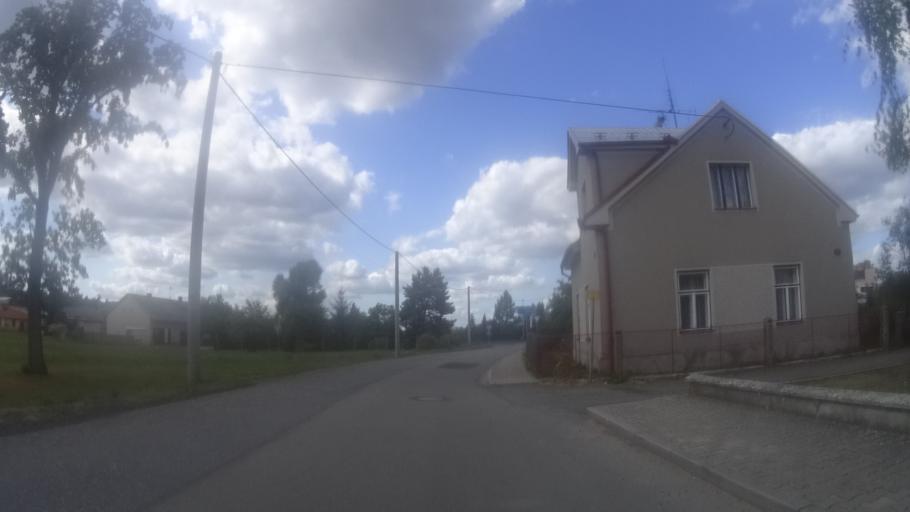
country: CZ
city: Borohradek
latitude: 50.0756
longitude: 16.1327
